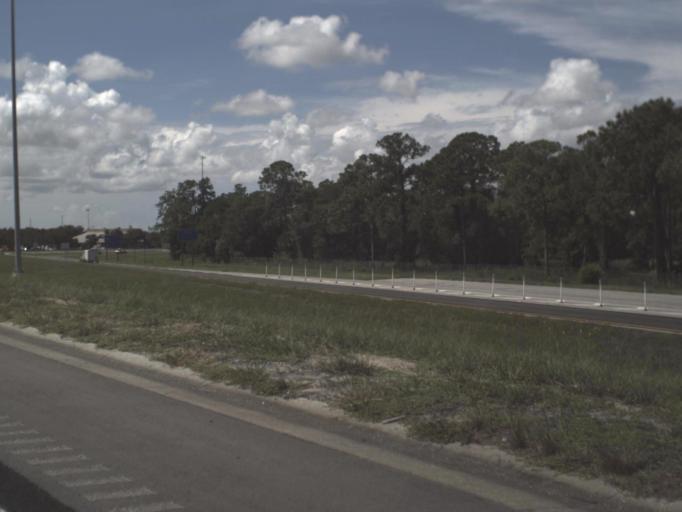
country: US
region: Florida
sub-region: Lee County
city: Tice
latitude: 26.6592
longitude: -81.7998
